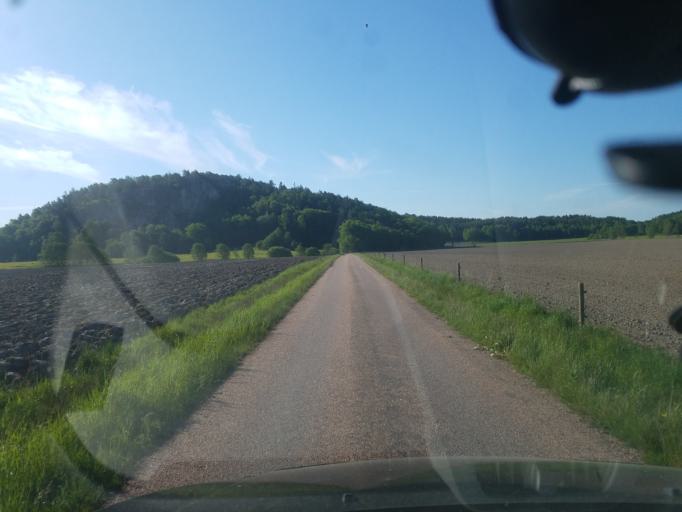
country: SE
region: Vaestra Goetaland
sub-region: Orust
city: Henan
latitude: 58.2894
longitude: 11.6375
